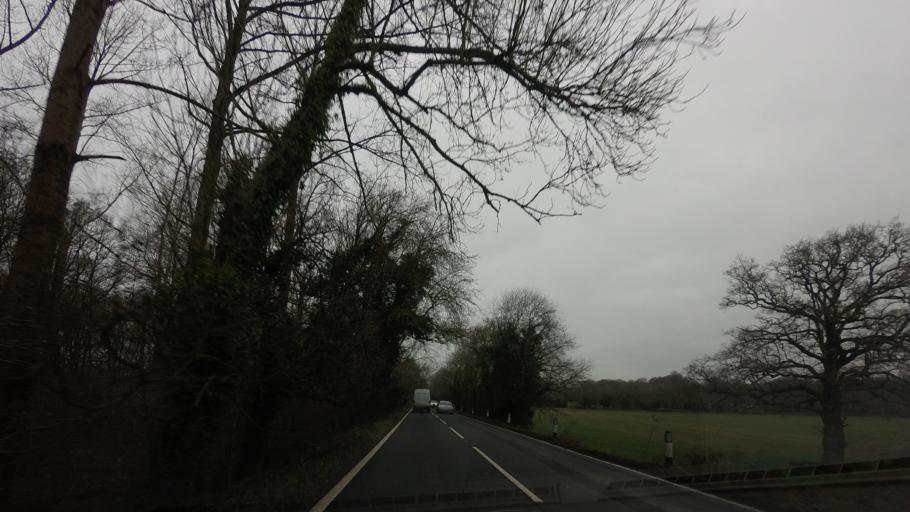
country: GB
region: England
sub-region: Kent
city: Staplehurst
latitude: 51.1310
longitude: 0.5600
